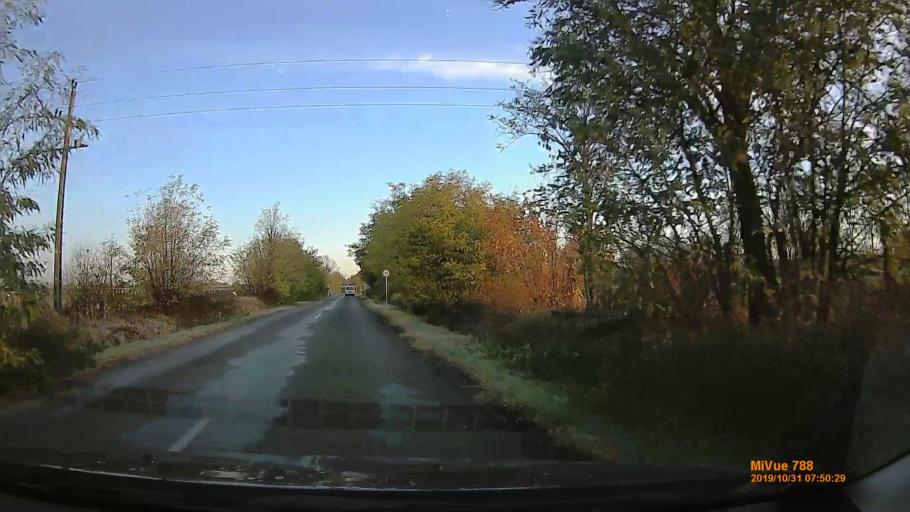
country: HU
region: Pest
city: Pilis
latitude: 47.3031
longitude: 19.5616
